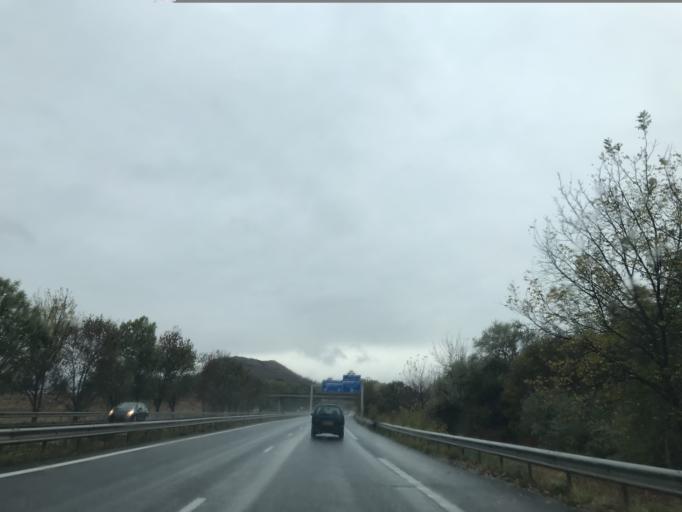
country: FR
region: Auvergne
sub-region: Departement du Puy-de-Dome
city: Aulnat
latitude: 45.7716
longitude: 3.1499
